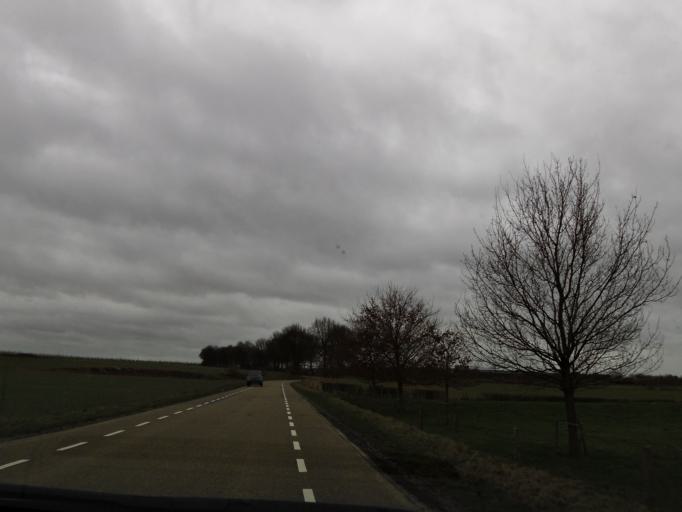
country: NL
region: Limburg
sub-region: Valkenburg aan de Geul
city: Sibbe
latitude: 50.8375
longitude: 5.8210
